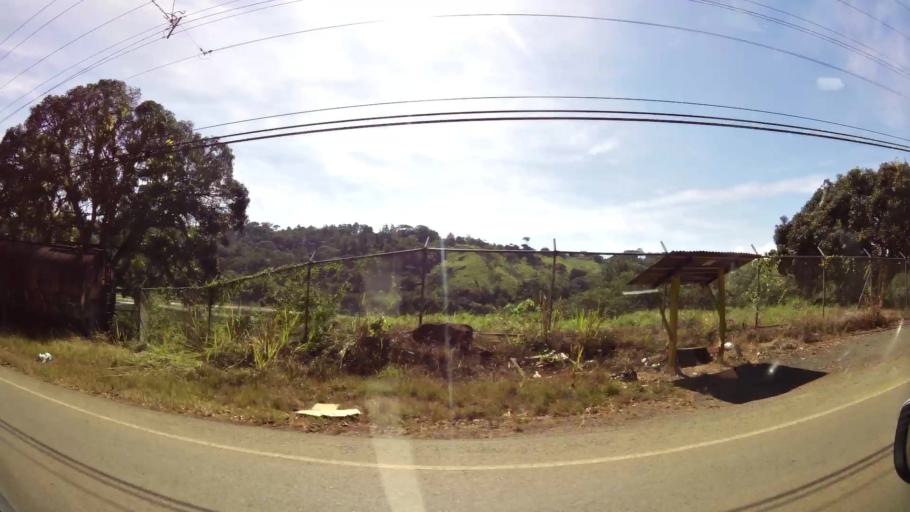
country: CR
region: San Jose
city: San Isidro
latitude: 9.3615
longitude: -83.7117
